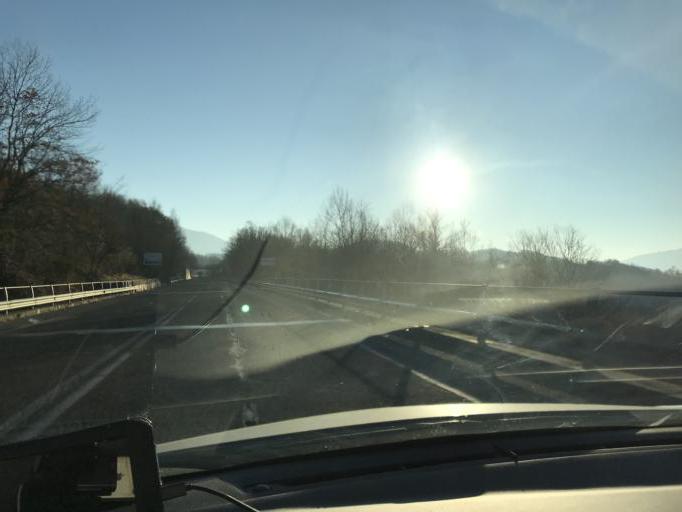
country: IT
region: Latium
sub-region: Provincia di Rieti
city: Fiamignano
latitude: 42.2587
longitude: 13.1180
